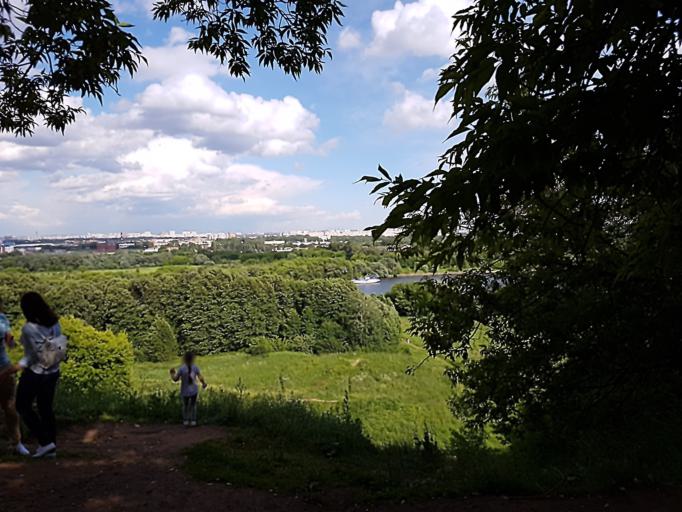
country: RU
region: Moscow
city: Kolomenskoye
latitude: 55.6617
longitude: 37.6663
